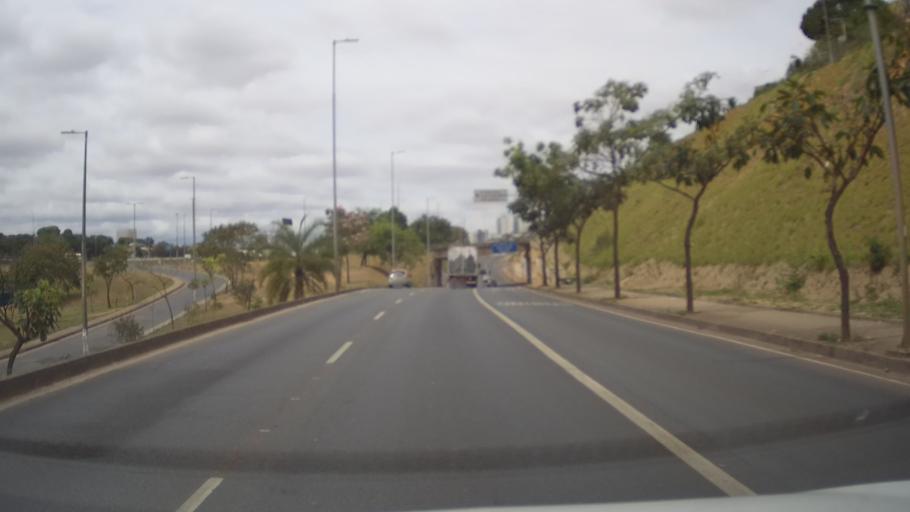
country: BR
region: Minas Gerais
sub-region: Belo Horizonte
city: Belo Horizonte
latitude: -19.8590
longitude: -43.9247
